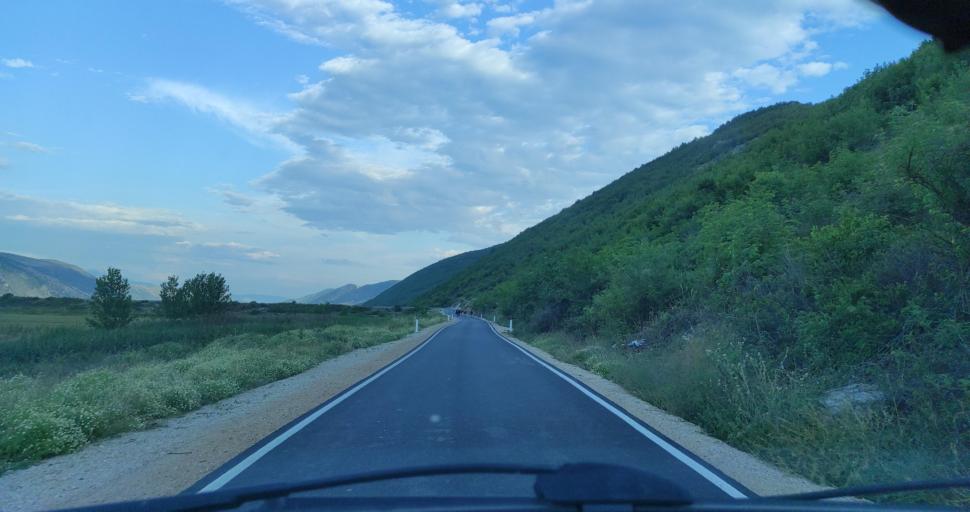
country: AL
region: Shkoder
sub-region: Rrethi i Shkodres
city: Velipoje
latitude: 41.9244
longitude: 19.4506
